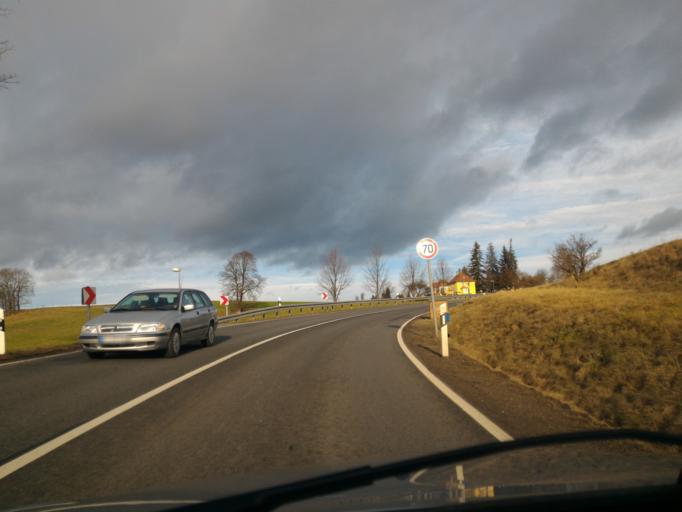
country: DE
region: Saxony
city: Neusalza-Spremberg
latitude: 51.0431
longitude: 14.5154
